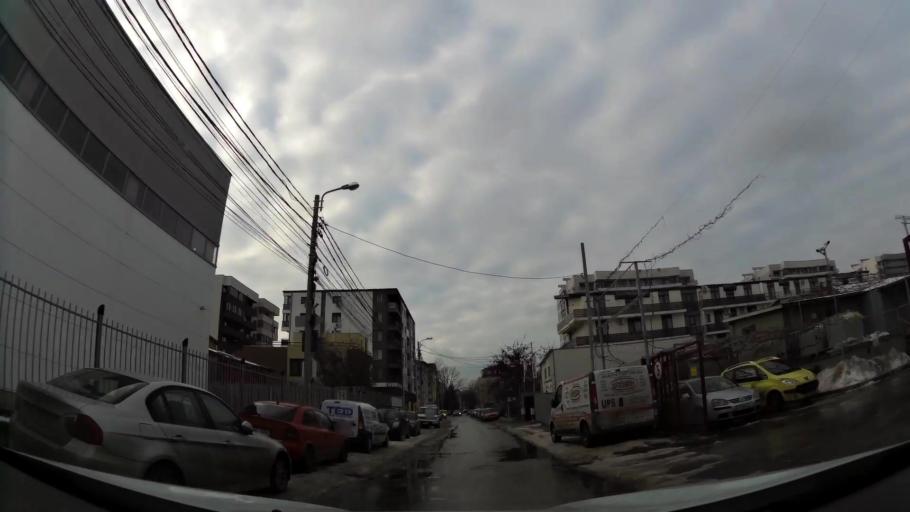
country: RO
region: Ilfov
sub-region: Comuna Popesti-Leordeni
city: Popesti-Leordeni
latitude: 44.4068
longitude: 26.1805
